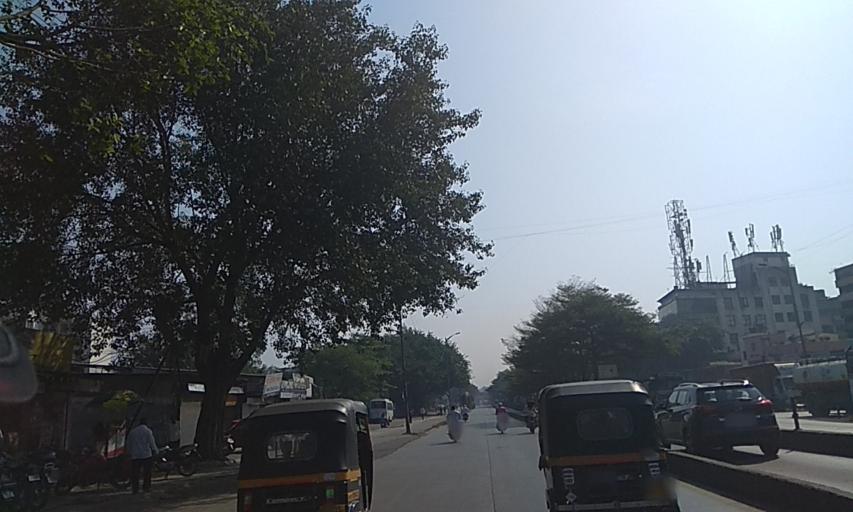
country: IN
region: Maharashtra
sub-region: Pune Division
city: Pune
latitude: 18.5039
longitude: 73.9223
